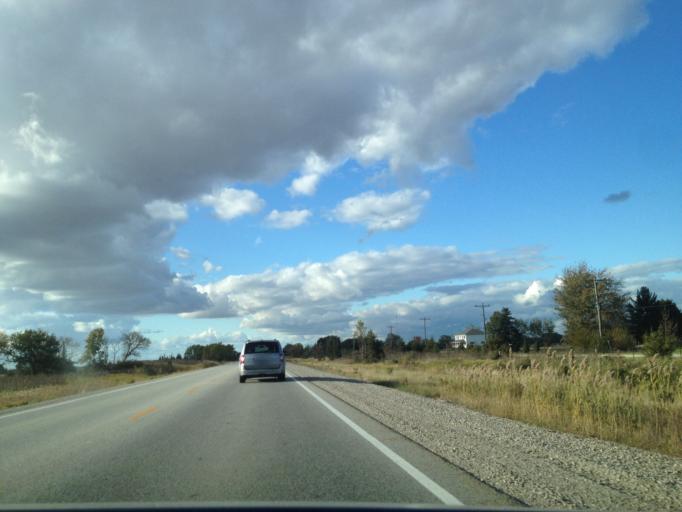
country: CA
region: Ontario
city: Amherstburg
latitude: 42.1107
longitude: -82.7463
